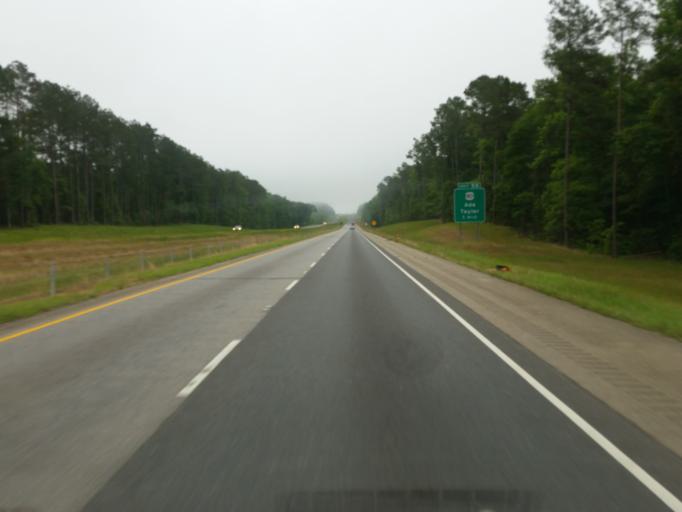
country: US
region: Louisiana
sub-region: Webster Parish
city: Minden
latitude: 32.5665
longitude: -93.1817
